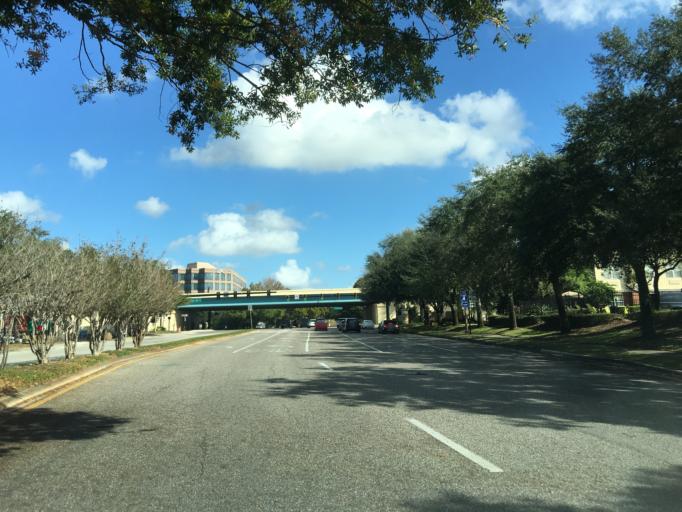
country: US
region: Florida
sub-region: Orange County
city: Eatonville
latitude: 28.6351
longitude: -81.4038
